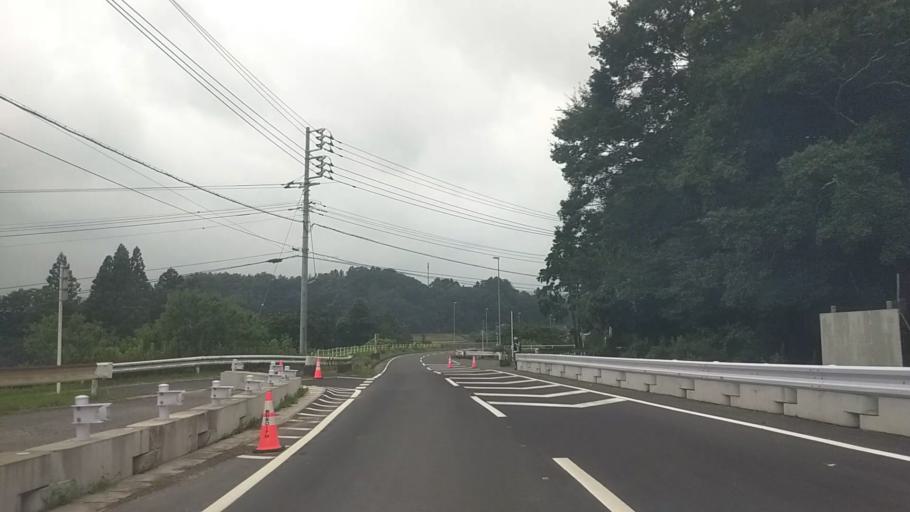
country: JP
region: Chiba
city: Kisarazu
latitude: 35.2608
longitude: 140.0485
